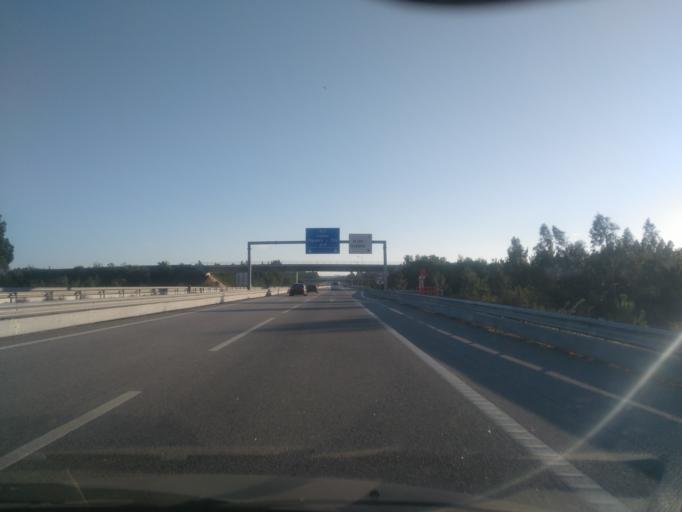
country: PT
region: Coimbra
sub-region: Figueira da Foz
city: Alhadas
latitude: 40.2254
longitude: -8.7941
